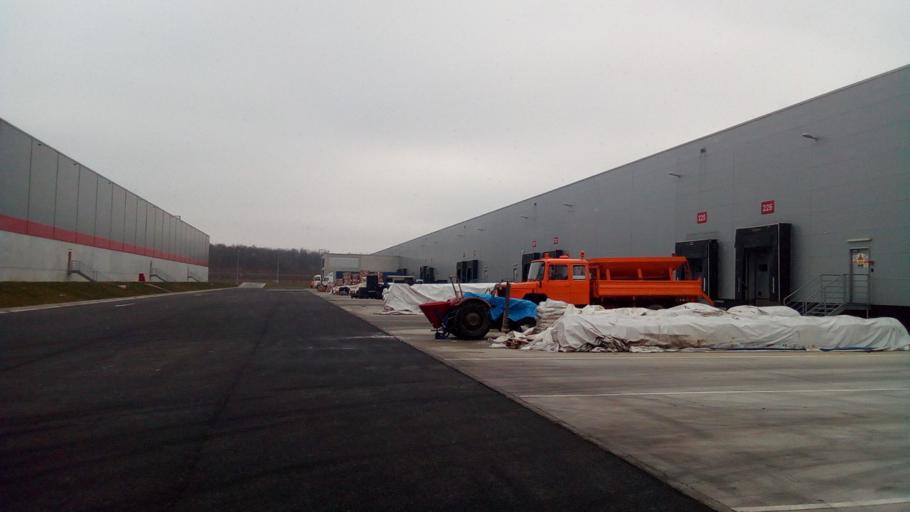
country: HR
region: Zagrebacka
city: Jastrebarsko
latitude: 45.6520
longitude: 15.6800
